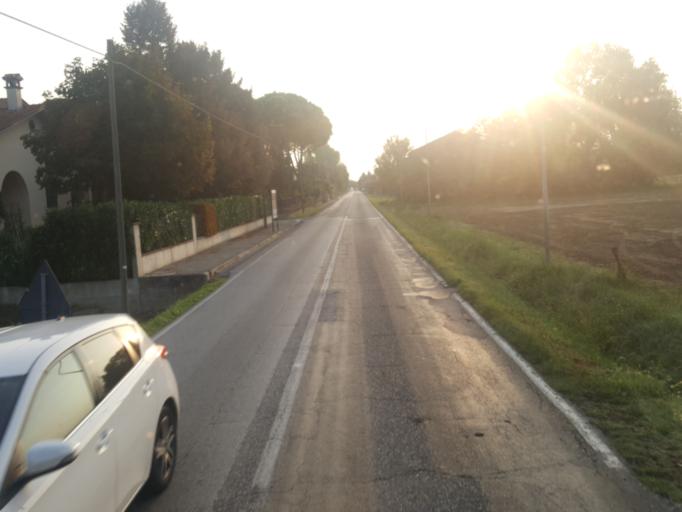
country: IT
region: Emilia-Romagna
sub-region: Provincia di Ravenna
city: Lavezzola
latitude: 44.5578
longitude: 11.8687
